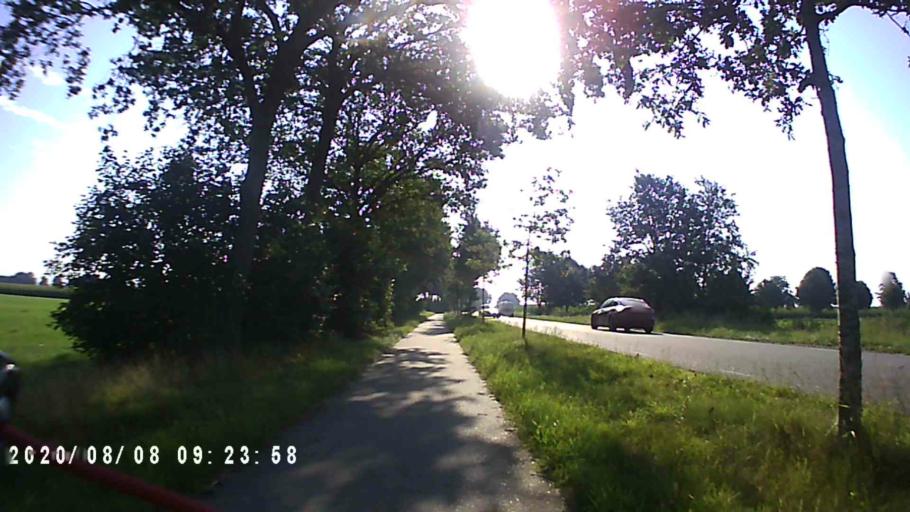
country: NL
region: Groningen
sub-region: Gemeente Leek
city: Leek
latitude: 53.0404
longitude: 6.3374
